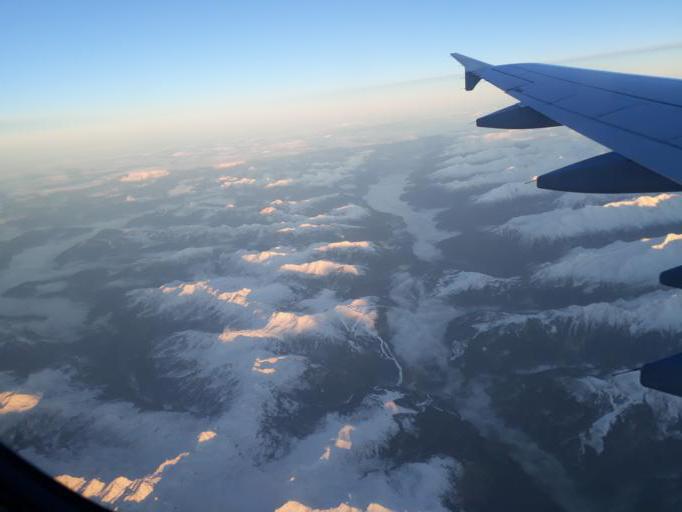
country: AT
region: Tyrol
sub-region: Politischer Bezirk Schwaz
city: Hainzenberg
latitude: 47.2275
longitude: 11.8989
